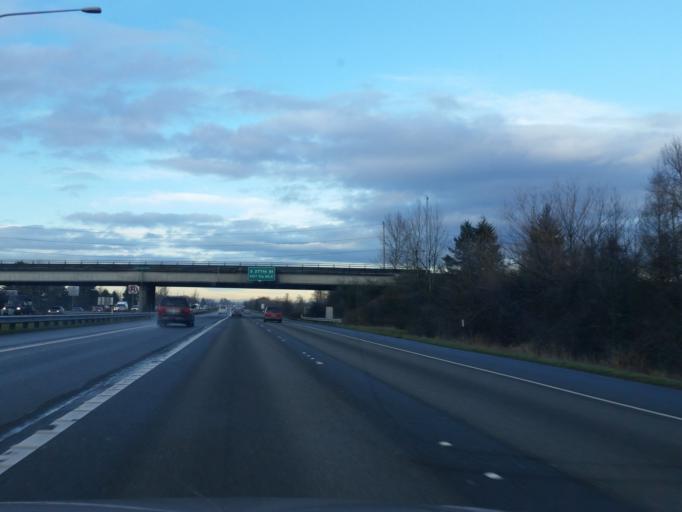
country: US
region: Washington
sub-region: King County
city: Lakeland North
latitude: 47.3390
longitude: -122.2446
